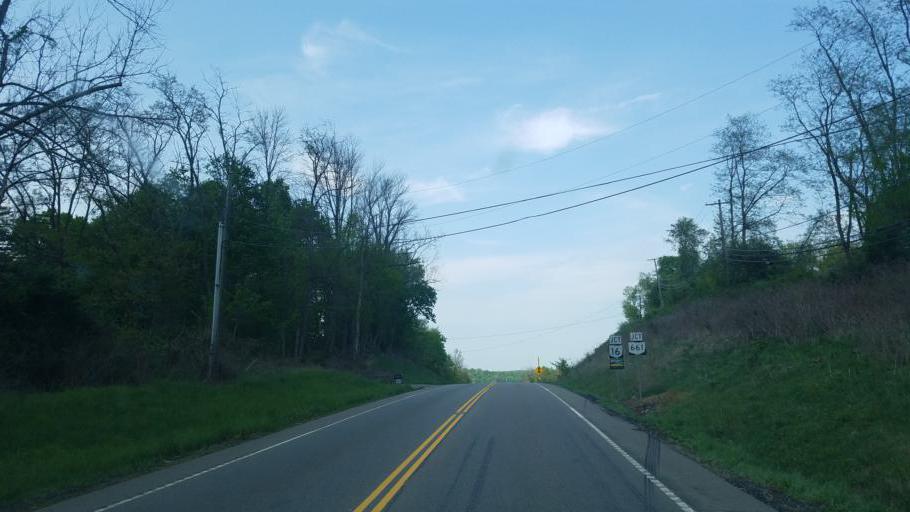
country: US
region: Ohio
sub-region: Licking County
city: Granville
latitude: 40.0537
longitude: -82.5220
